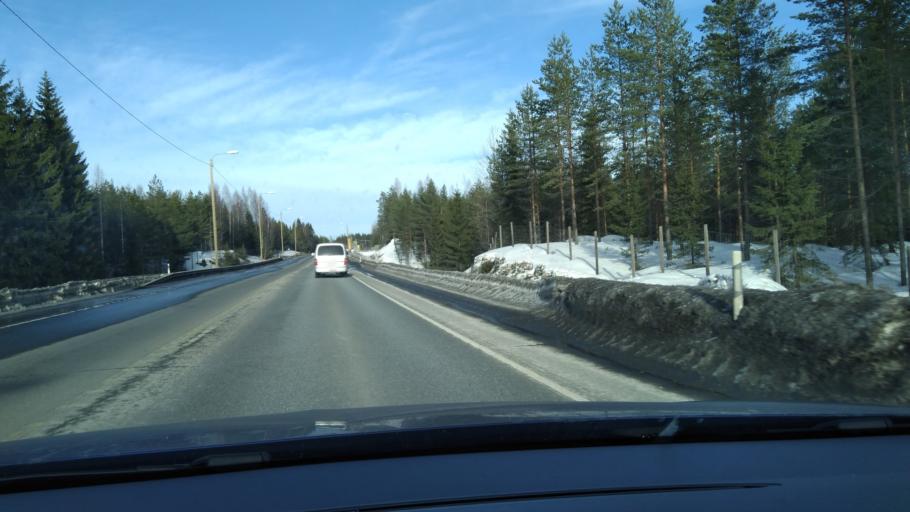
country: FI
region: Pirkanmaa
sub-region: Tampere
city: Orivesi
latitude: 61.6672
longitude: 24.2750
